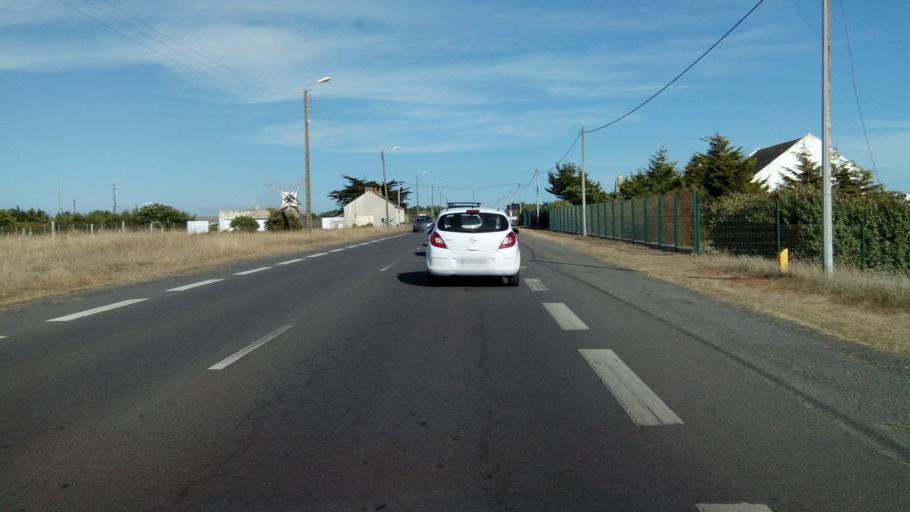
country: FR
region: Pays de la Loire
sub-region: Departement de la Loire-Atlantique
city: Batz-sur-Mer
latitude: 47.2807
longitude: -2.4927
